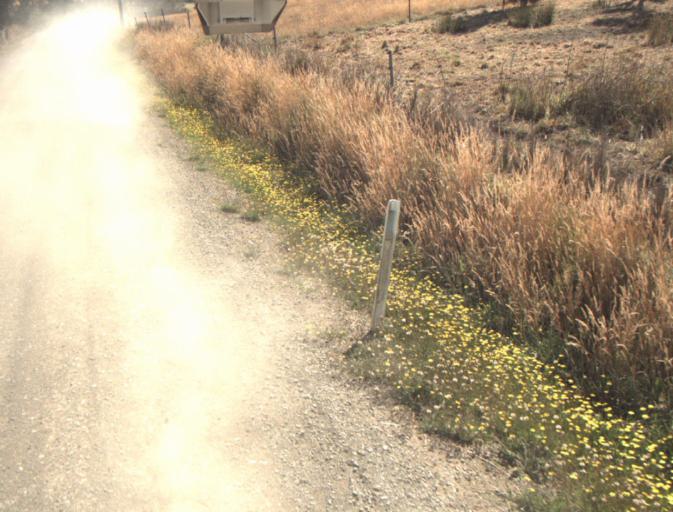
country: AU
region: Tasmania
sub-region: Launceston
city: Mayfield
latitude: -41.2257
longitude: 147.2367
